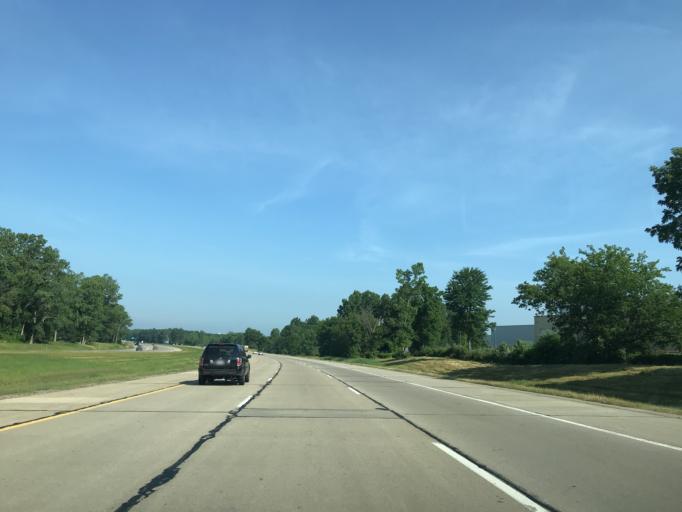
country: US
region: Michigan
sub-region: Livingston County
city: Howell
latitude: 42.6024
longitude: -83.9495
